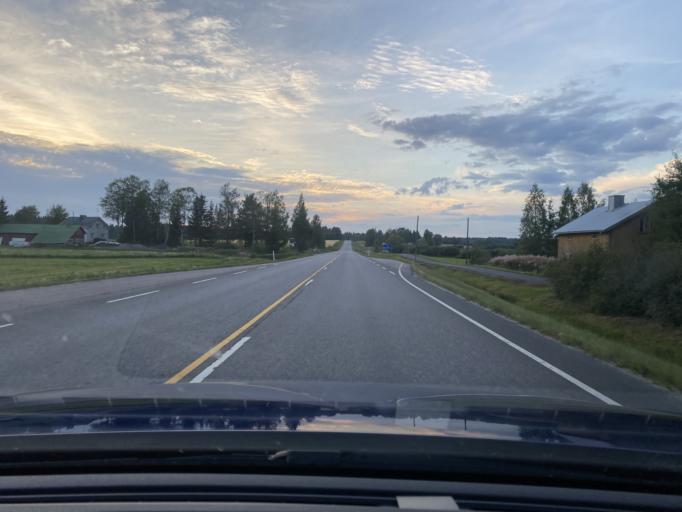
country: FI
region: Satakunta
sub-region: Pohjois-Satakunta
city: Kankaanpaeae
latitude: 61.7479
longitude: 22.5190
